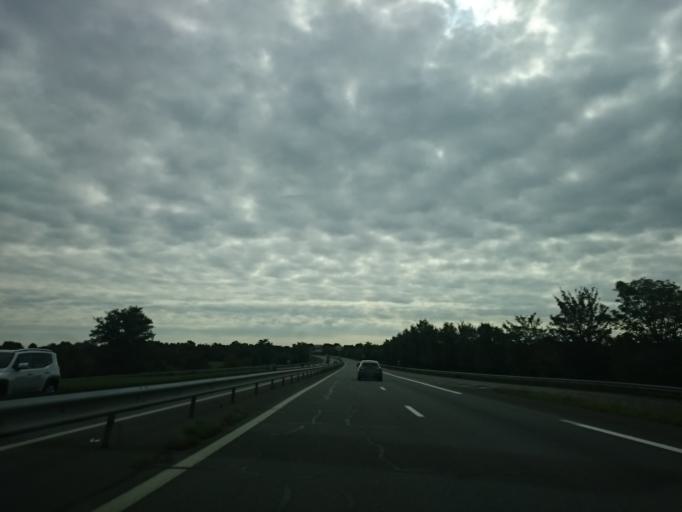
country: FR
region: Pays de la Loire
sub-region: Departement de la Loire-Atlantique
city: La Chapelle-Launay
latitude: 47.3814
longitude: -1.9646
